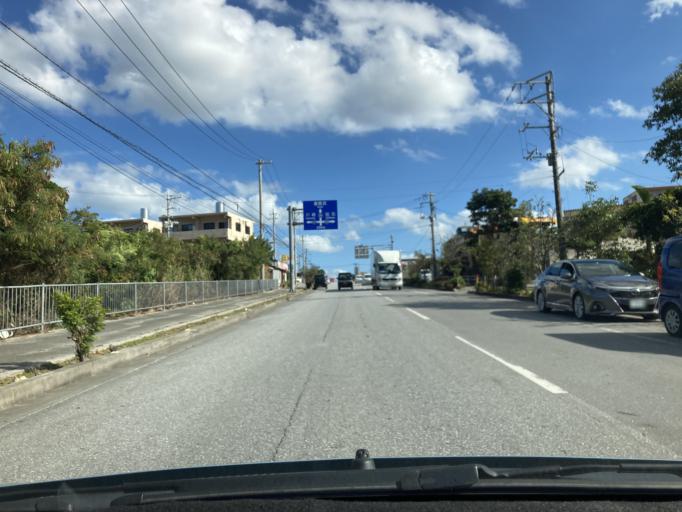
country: JP
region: Okinawa
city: Okinawa
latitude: 26.3741
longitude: 127.8235
